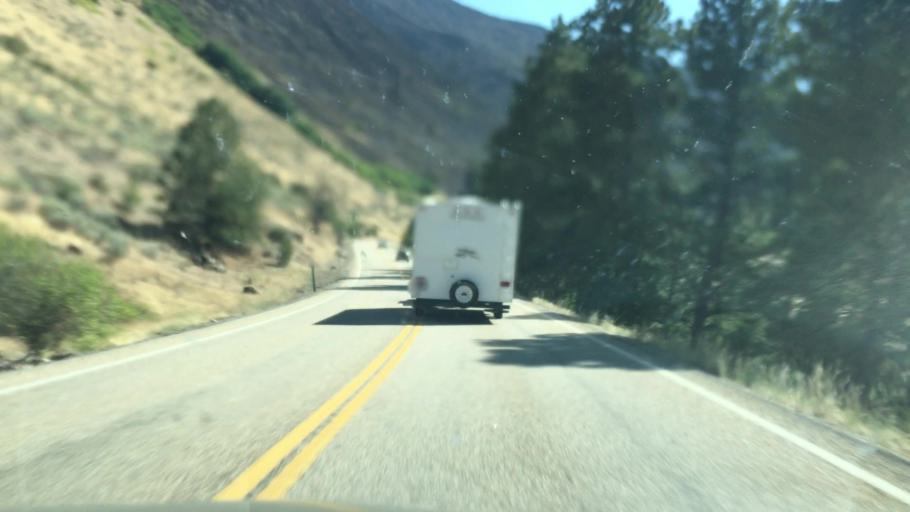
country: US
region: Idaho
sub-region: Boise County
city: Idaho City
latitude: 44.0201
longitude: -116.1516
